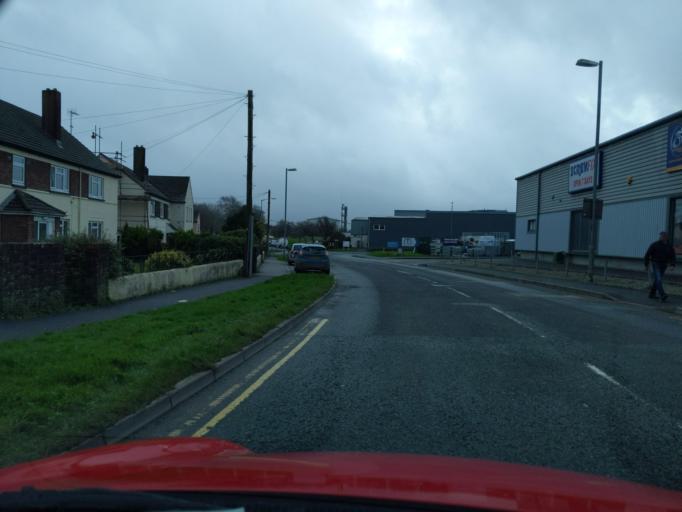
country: GB
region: England
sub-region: Cornwall
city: Launceston
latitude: 50.6268
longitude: -4.3571
